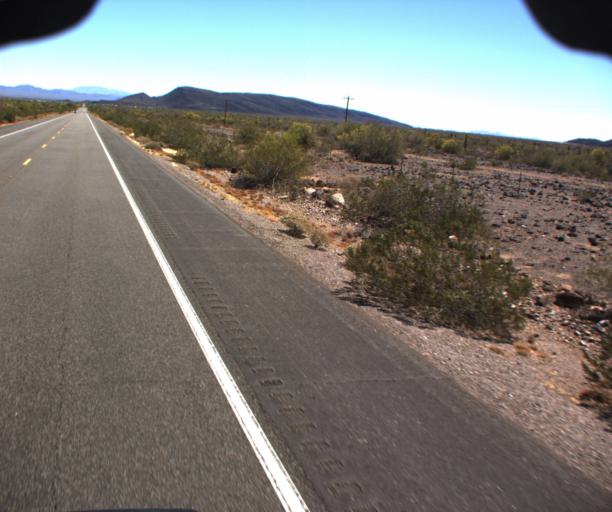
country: US
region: Arizona
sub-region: La Paz County
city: Quartzsite
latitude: 33.6680
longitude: -113.9924
